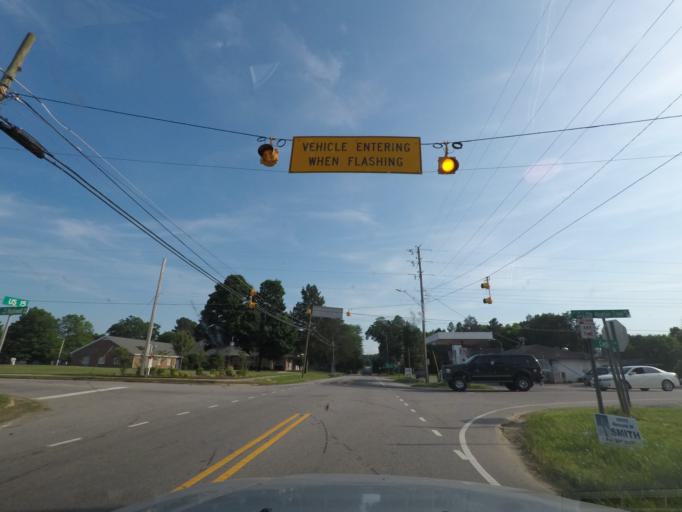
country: US
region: North Carolina
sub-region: Granville County
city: Oxford
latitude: 36.4479
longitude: -78.5701
